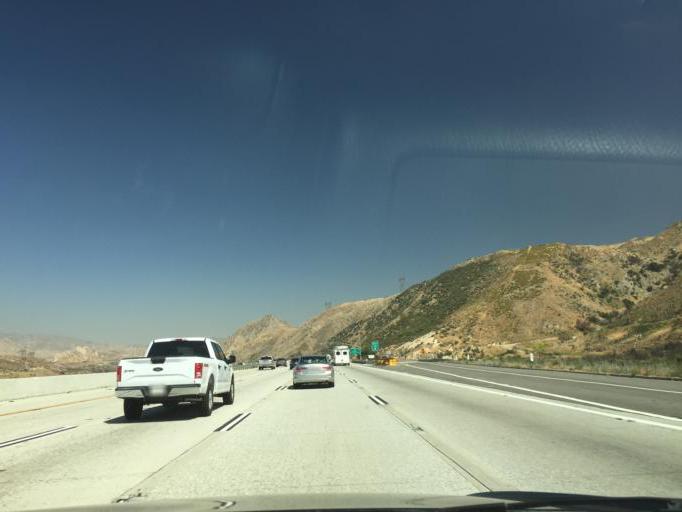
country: US
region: California
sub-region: San Bernardino County
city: Oak Hills
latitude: 34.2961
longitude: -117.4552
